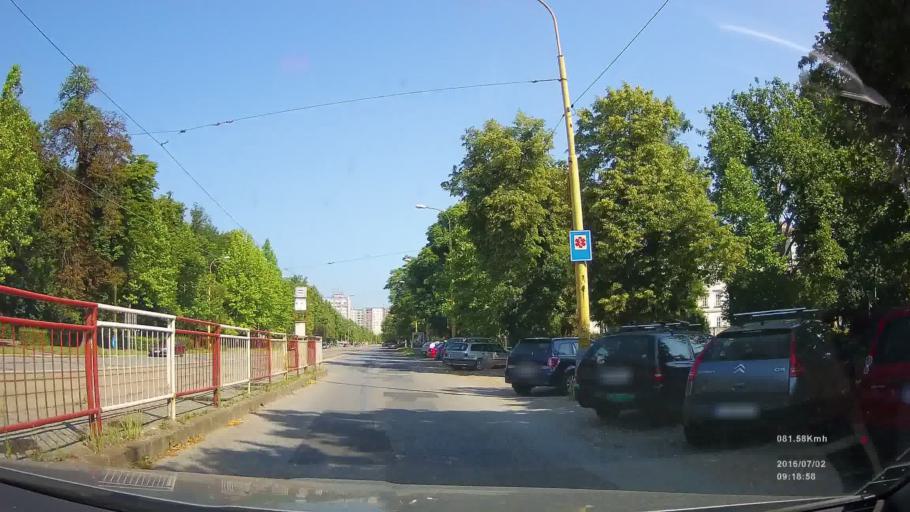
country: SK
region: Kosicky
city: Kosice
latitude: 48.7344
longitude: 21.2338
